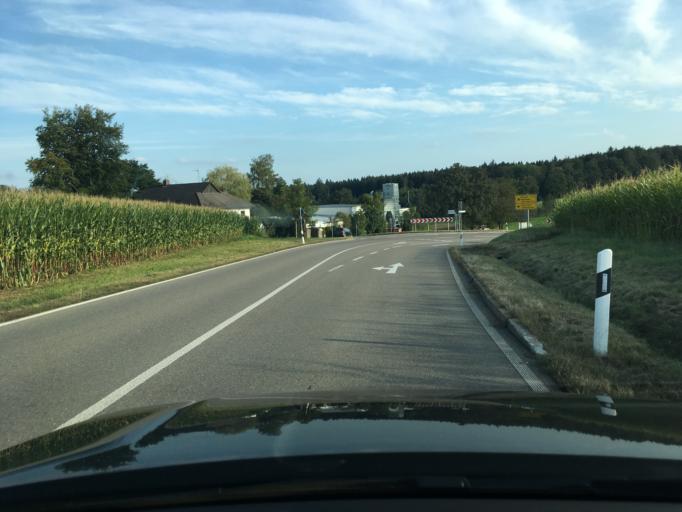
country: DE
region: Baden-Wuerttemberg
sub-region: Regierungsbezirk Stuttgart
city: Adelberg
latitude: 48.7651
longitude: 9.5669
